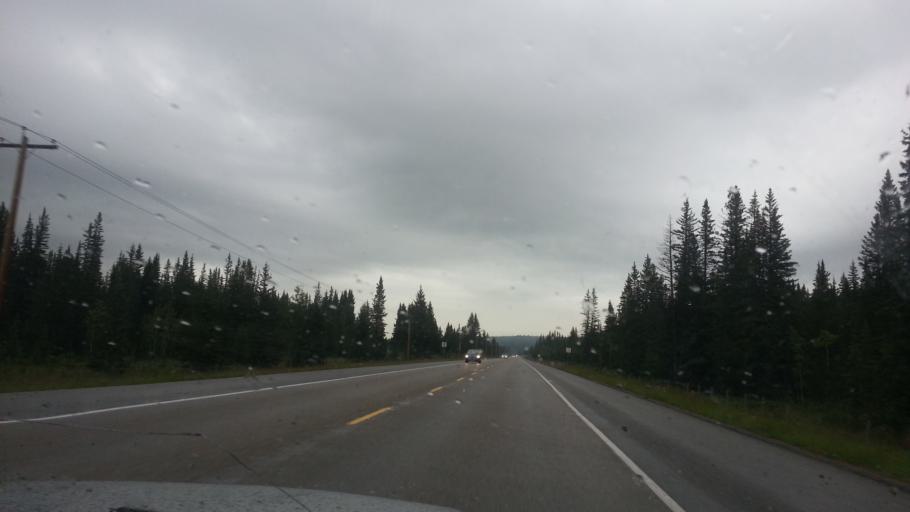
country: CA
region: Alberta
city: Cochrane
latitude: 50.9716
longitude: -114.5344
